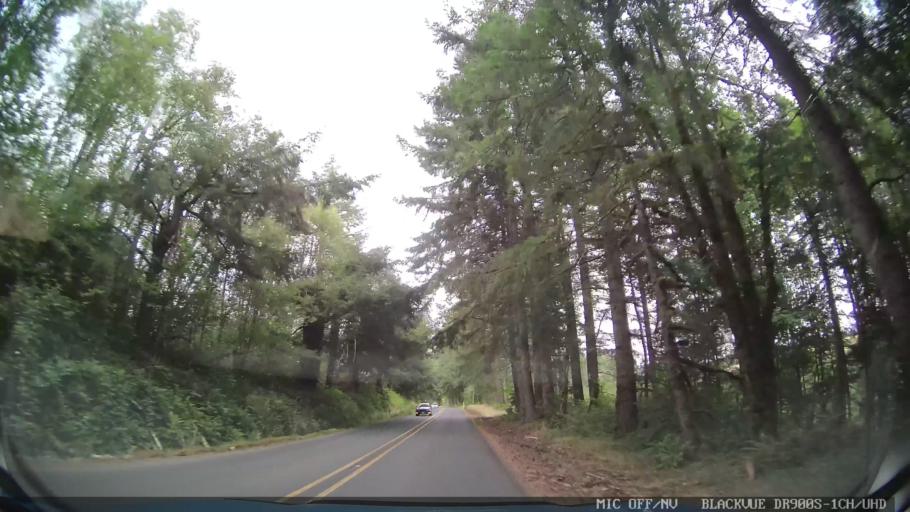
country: US
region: Oregon
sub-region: Linn County
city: Lyons
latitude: 44.8486
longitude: -122.6716
